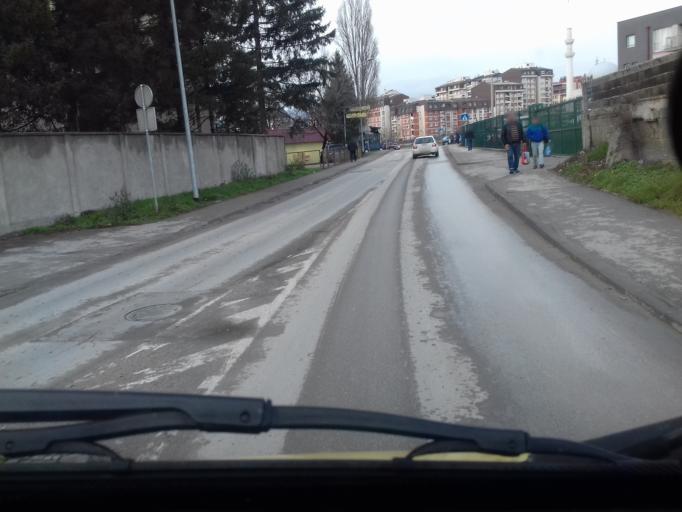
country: BA
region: Federation of Bosnia and Herzegovina
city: Zenica
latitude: 44.1925
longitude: 17.9335
